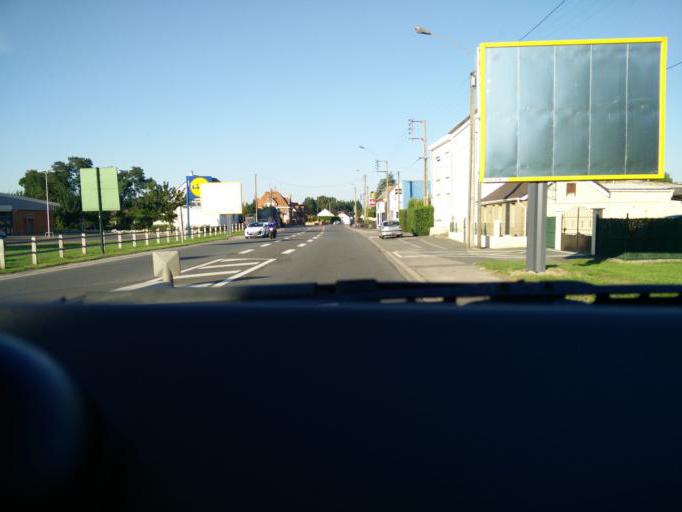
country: FR
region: Nord-Pas-de-Calais
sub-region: Departement du Pas-de-Calais
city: Auchy-les-Mines
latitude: 50.5203
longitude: 2.7916
